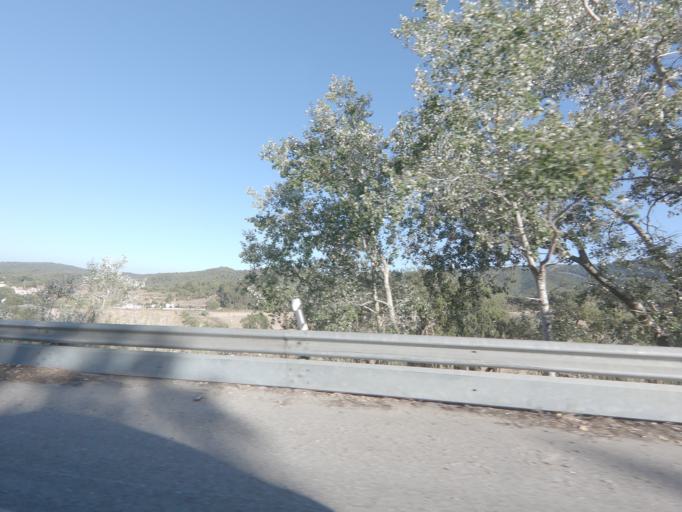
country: PT
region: Setubal
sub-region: Palmela
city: Quinta do Anjo
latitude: 38.5163
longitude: -8.9762
